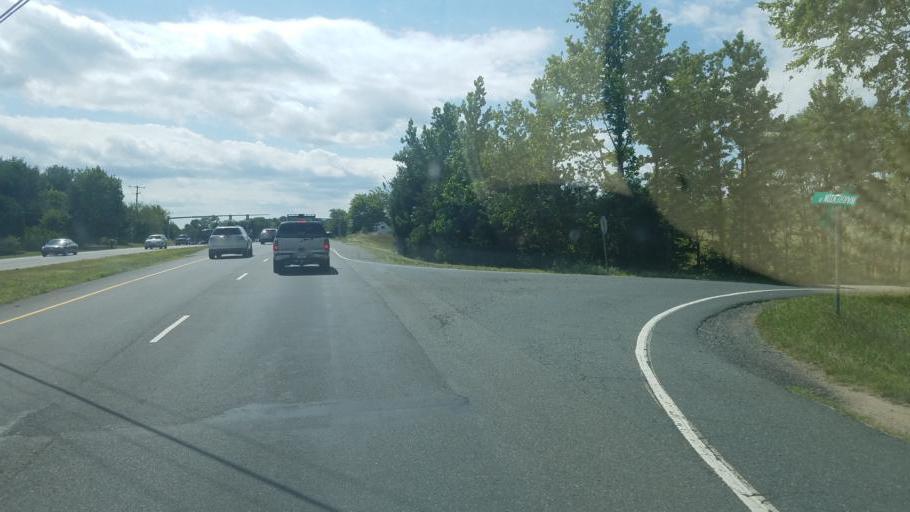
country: US
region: Virginia
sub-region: Stafford County
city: Falmouth
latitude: 38.3831
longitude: -77.5445
